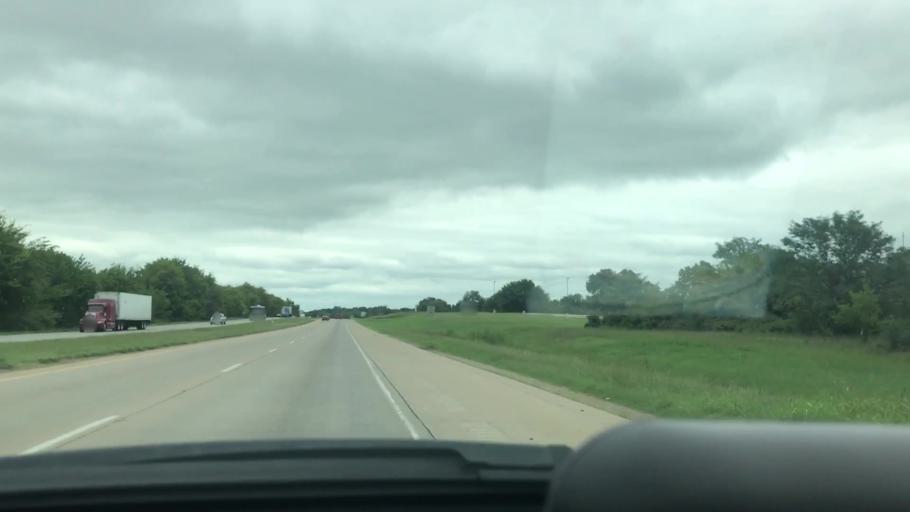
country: US
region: Oklahoma
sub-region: Mayes County
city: Chouteau
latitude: 36.1926
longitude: -95.3419
